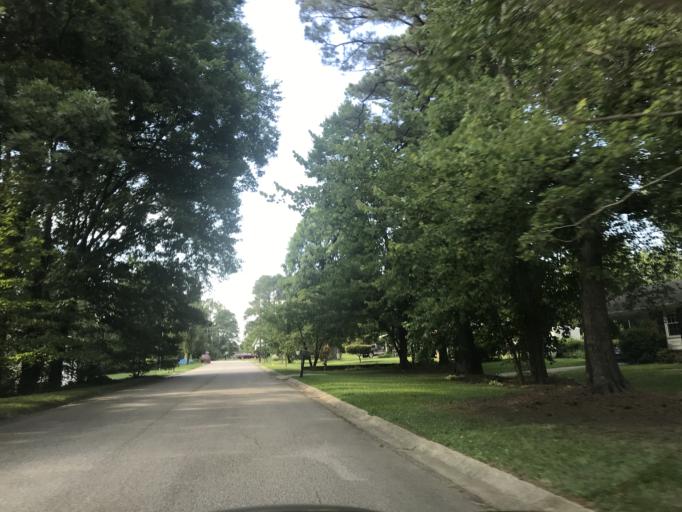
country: US
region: North Carolina
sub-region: Wake County
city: Raleigh
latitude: 35.8281
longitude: -78.5825
